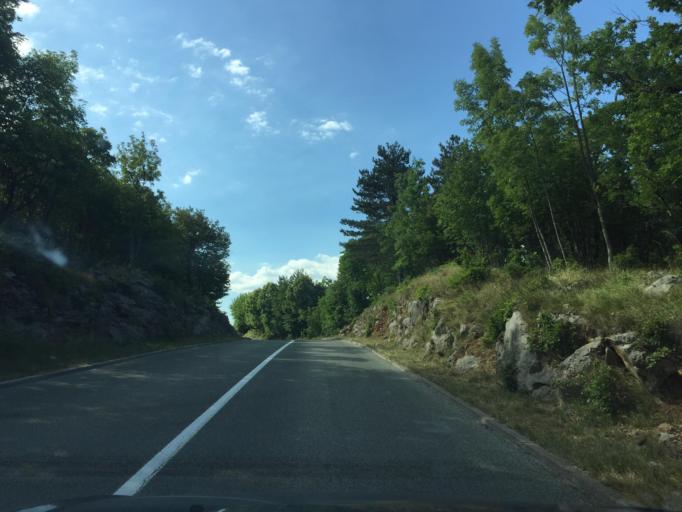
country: HR
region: Primorsko-Goranska
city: Klana
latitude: 45.4491
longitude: 14.3232
